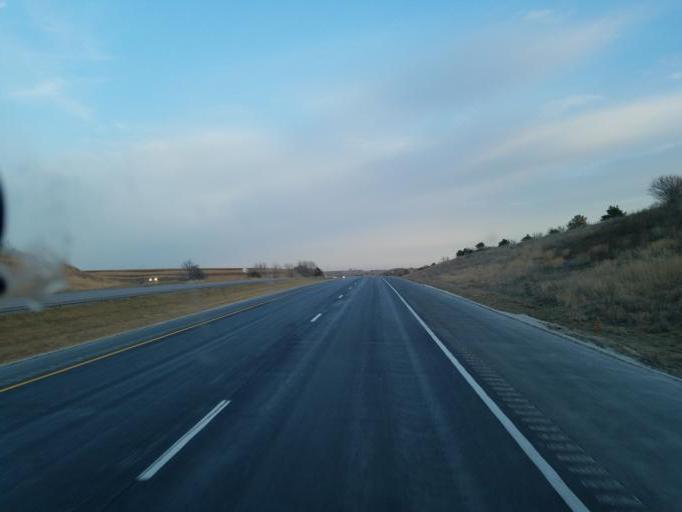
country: US
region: Iowa
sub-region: Harrison County
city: Missouri Valley
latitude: 41.4986
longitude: -95.7522
